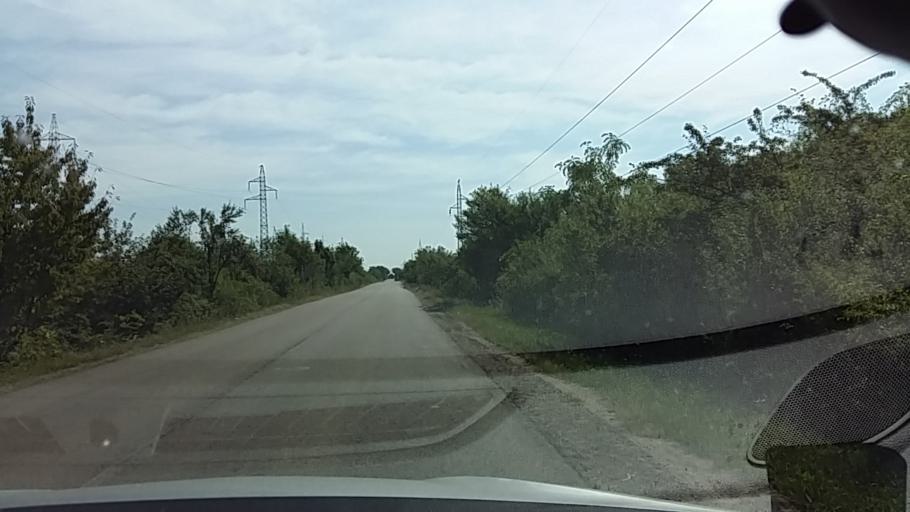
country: HU
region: Heves
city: Domoszlo
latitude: 47.7721
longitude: 20.0990
